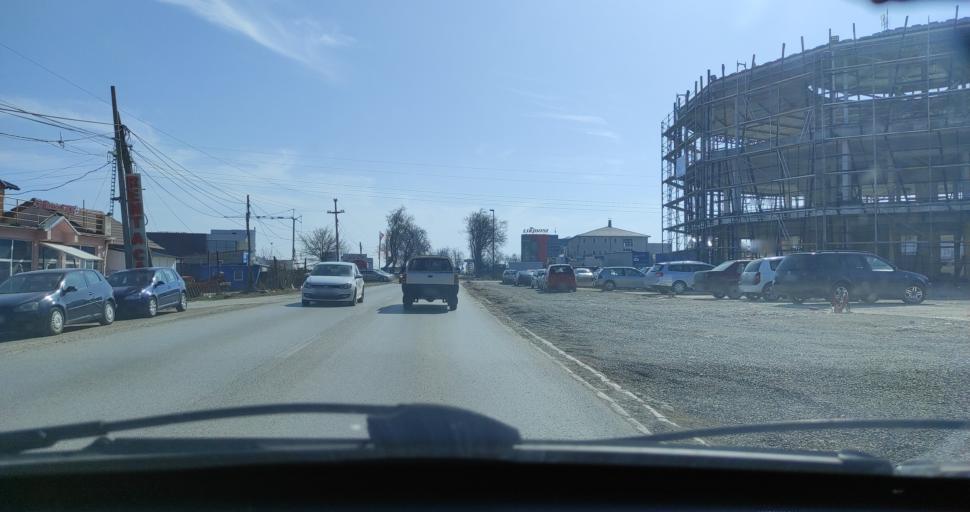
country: XK
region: Pec
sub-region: Komuna e Pejes
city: Peje
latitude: 42.6342
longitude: 20.3018
